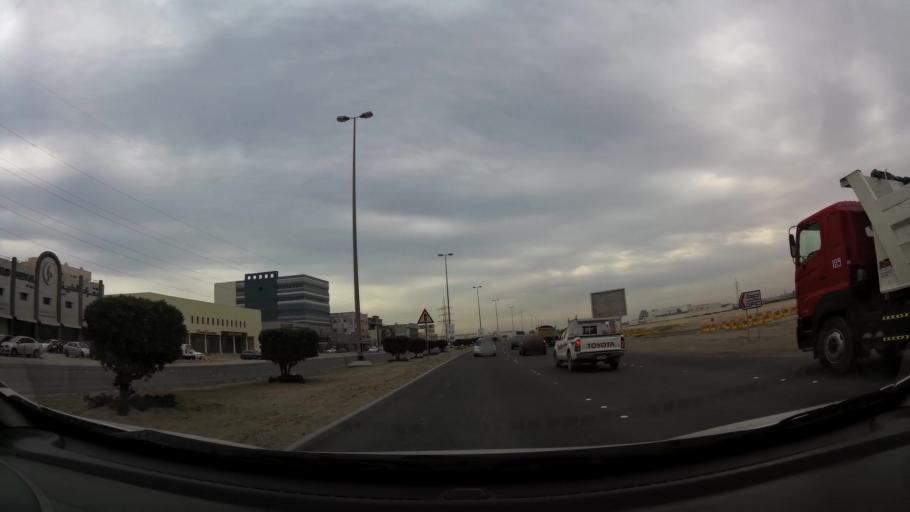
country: BH
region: Northern
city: Sitrah
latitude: 26.1506
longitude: 50.6175
